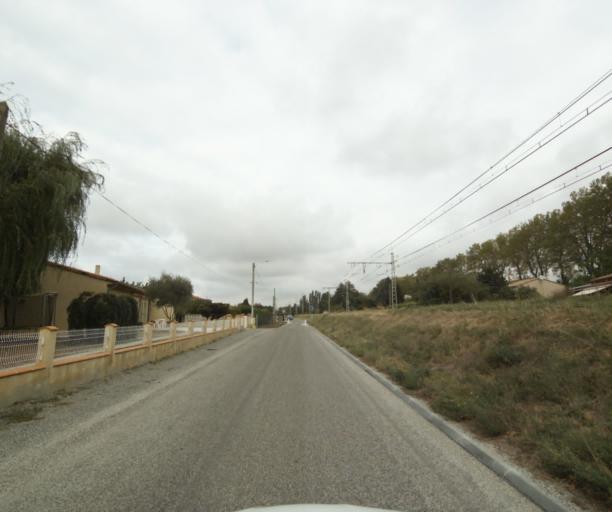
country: FR
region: Midi-Pyrenees
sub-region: Departement de la Haute-Garonne
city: Villefranche-de-Lauragais
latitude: 43.3917
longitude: 1.7236
